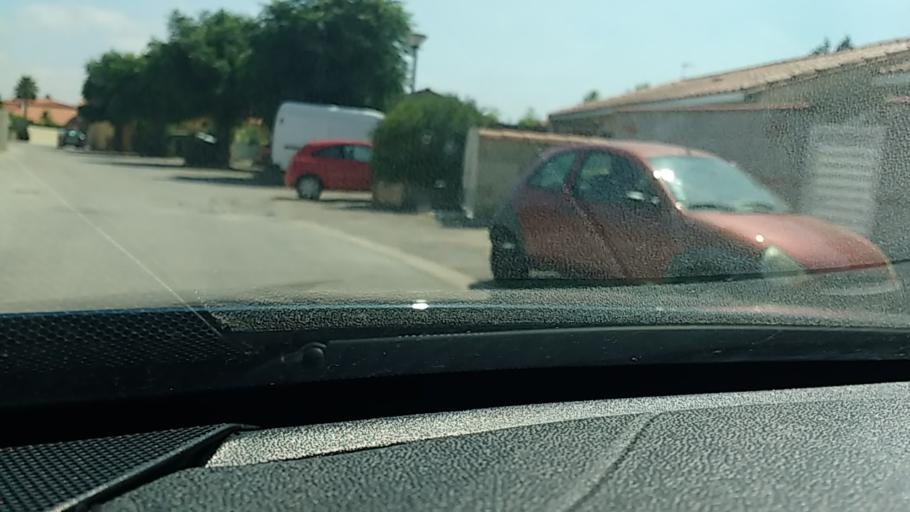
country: FR
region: Languedoc-Roussillon
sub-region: Departement des Pyrenees-Orientales
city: Villeneuve-de-la-Raho
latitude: 42.6328
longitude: 2.9186
